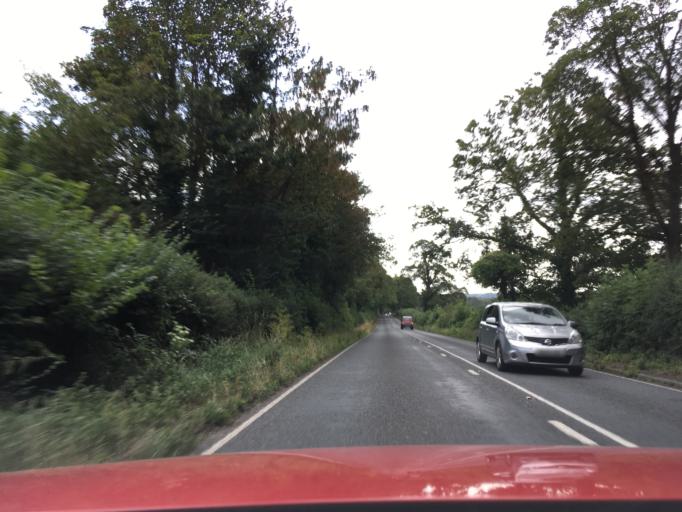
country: GB
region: England
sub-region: Hampshire
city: Kings Worthy
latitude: 51.0971
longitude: -1.2888
